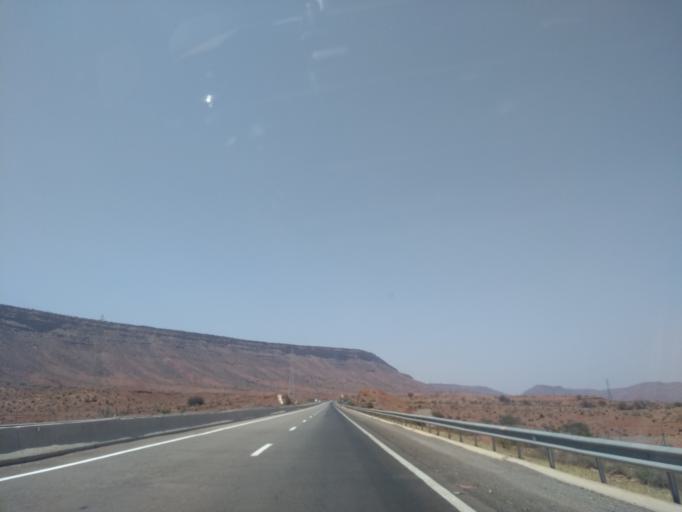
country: MA
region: Marrakech-Tensift-Al Haouz
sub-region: Chichaoua
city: Timezgadiouine
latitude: 30.9149
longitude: -9.0708
